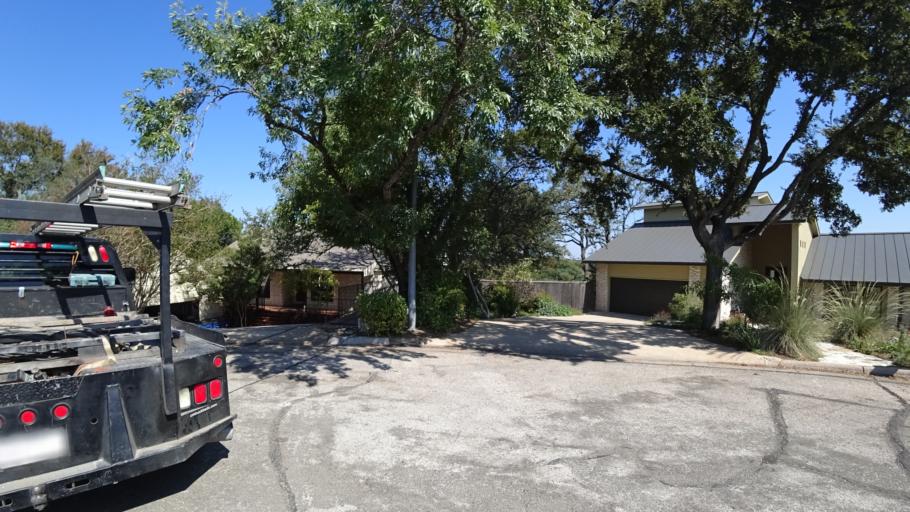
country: US
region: Texas
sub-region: Travis County
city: Rollingwood
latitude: 30.2499
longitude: -97.7893
